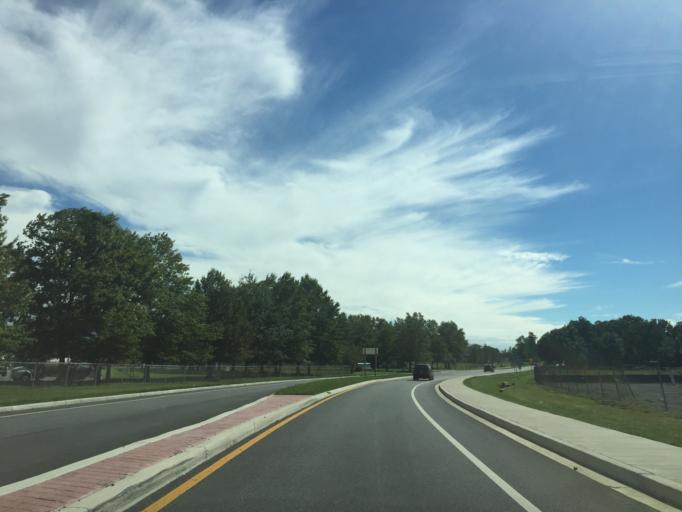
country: US
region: Maryland
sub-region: Baltimore County
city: Middle River
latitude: 39.3296
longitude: -76.4247
